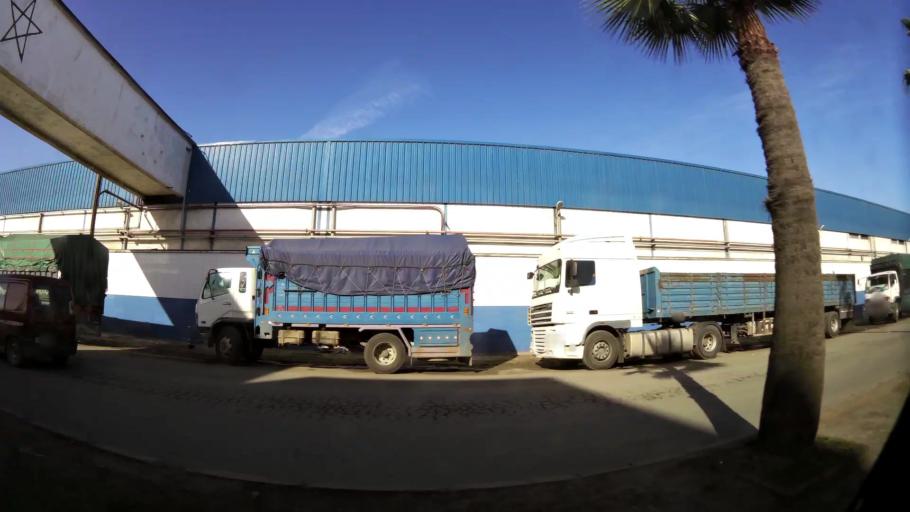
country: MA
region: Grand Casablanca
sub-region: Casablanca
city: Casablanca
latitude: 33.6028
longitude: -7.5740
